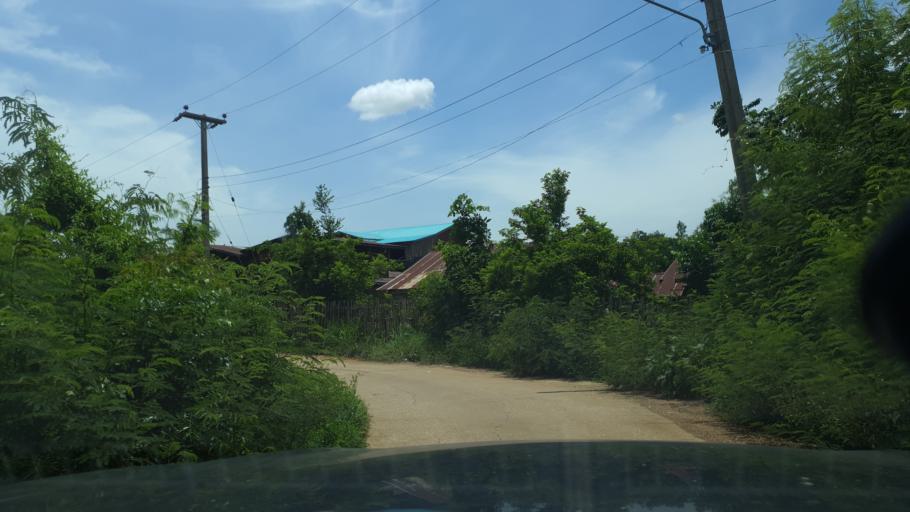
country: TH
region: Sukhothai
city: Ban Na
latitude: 17.0928
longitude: 99.6874
